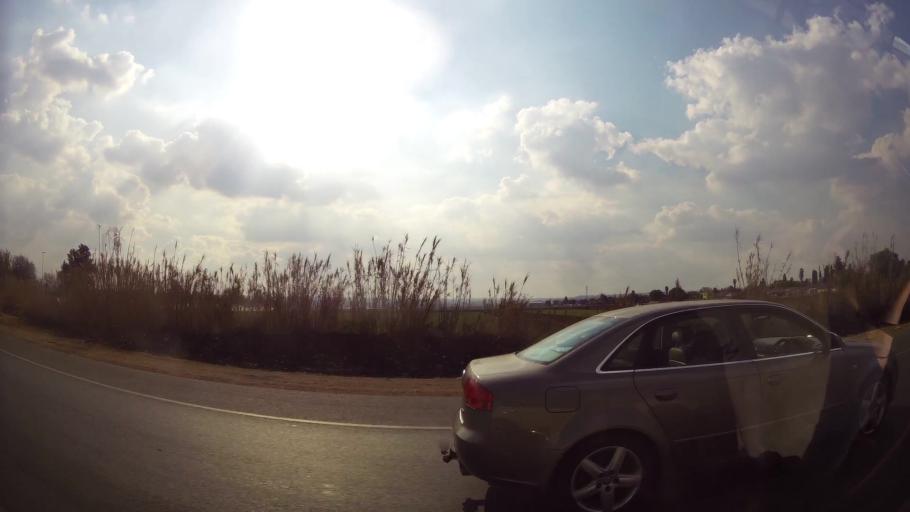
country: ZA
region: Gauteng
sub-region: Ekurhuleni Metropolitan Municipality
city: Germiston
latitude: -26.2942
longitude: 28.2129
